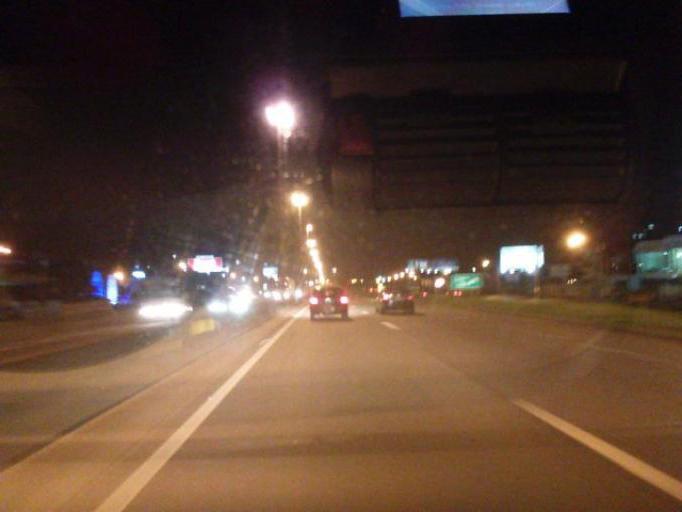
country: BR
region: Santa Catarina
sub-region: Balneario Camboriu
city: Balneario Camboriu
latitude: -26.9979
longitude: -48.6509
